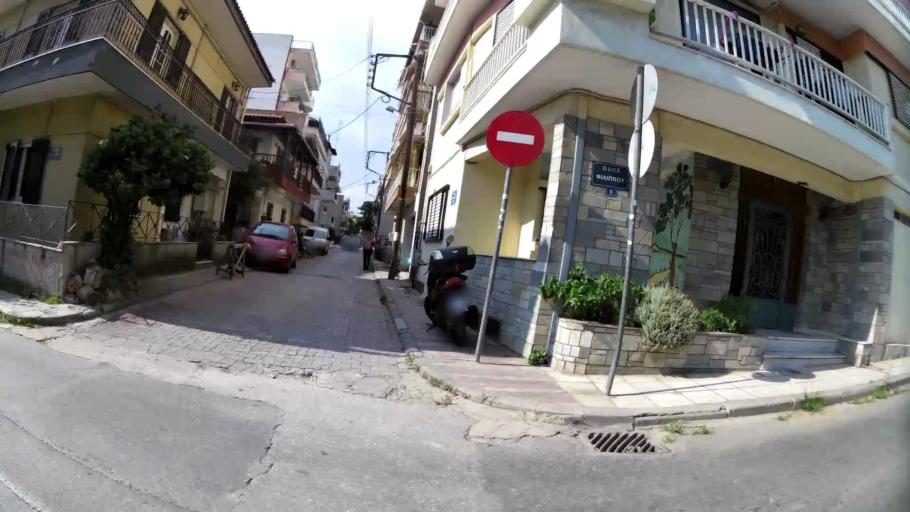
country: GR
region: Central Macedonia
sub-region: Nomos Thessalonikis
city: Polichni
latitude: 40.6597
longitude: 22.9480
